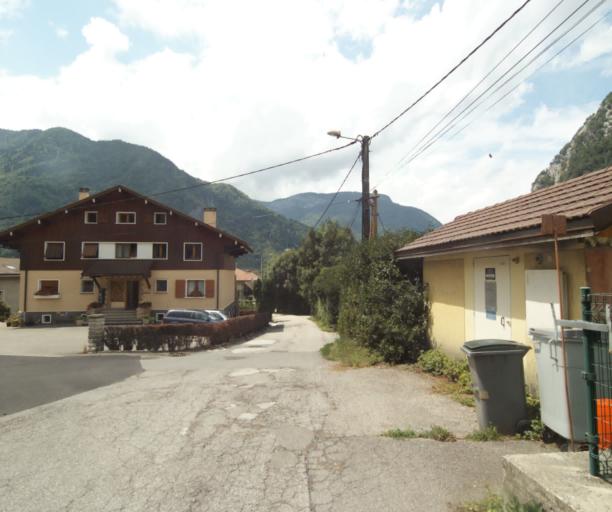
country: FR
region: Rhone-Alpes
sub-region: Departement de la Haute-Savoie
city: Thones
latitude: 45.8817
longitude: 6.3289
